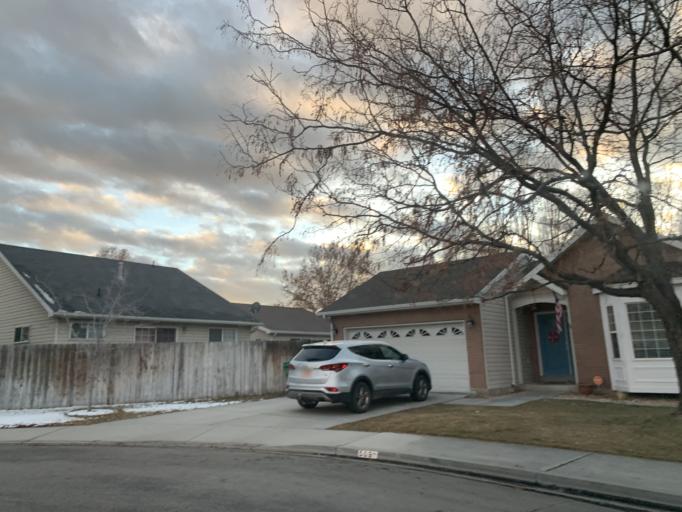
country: US
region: Utah
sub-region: Utah County
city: Provo
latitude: 40.2407
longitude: -111.6973
